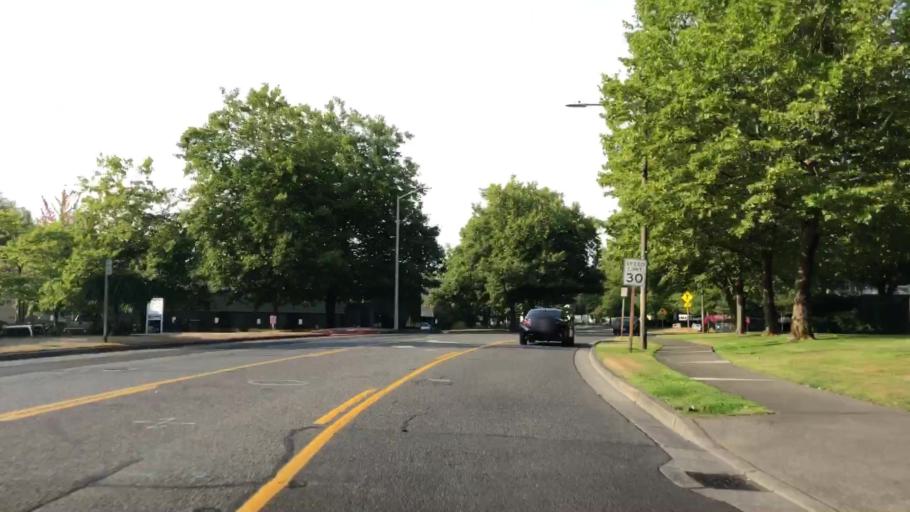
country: US
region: Washington
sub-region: Snohomish County
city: Mill Creek
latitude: 47.8528
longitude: -122.2209
